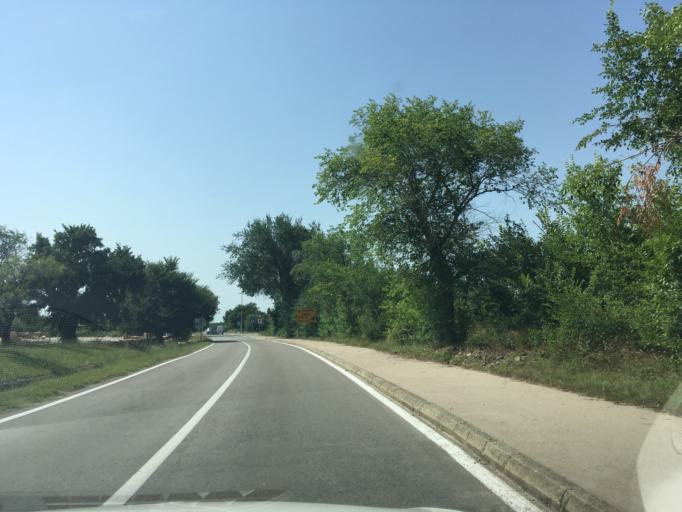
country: HR
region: Zadarska
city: Benkovac
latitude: 44.0273
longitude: 15.6141
